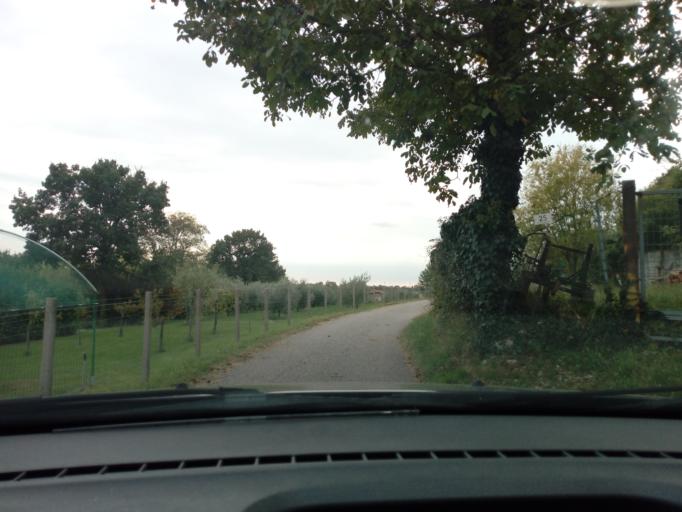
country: IT
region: Friuli Venezia Giulia
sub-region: Provincia di Udine
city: Cividale del Friuli
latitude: 46.0848
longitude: 13.4437
